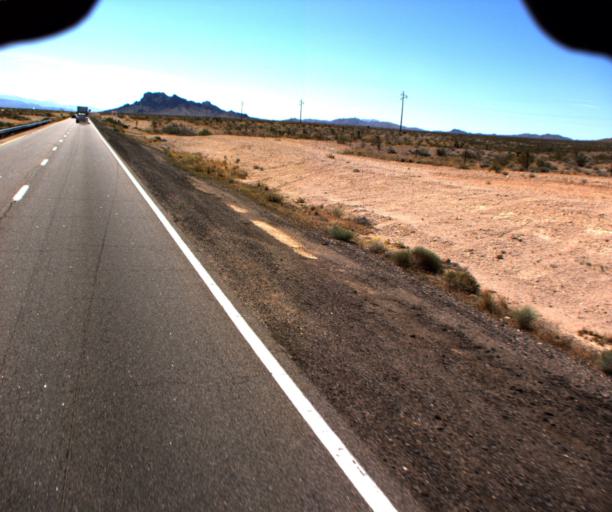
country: US
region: Nevada
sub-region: Clark County
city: Boulder City
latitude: 35.8343
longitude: -114.5655
